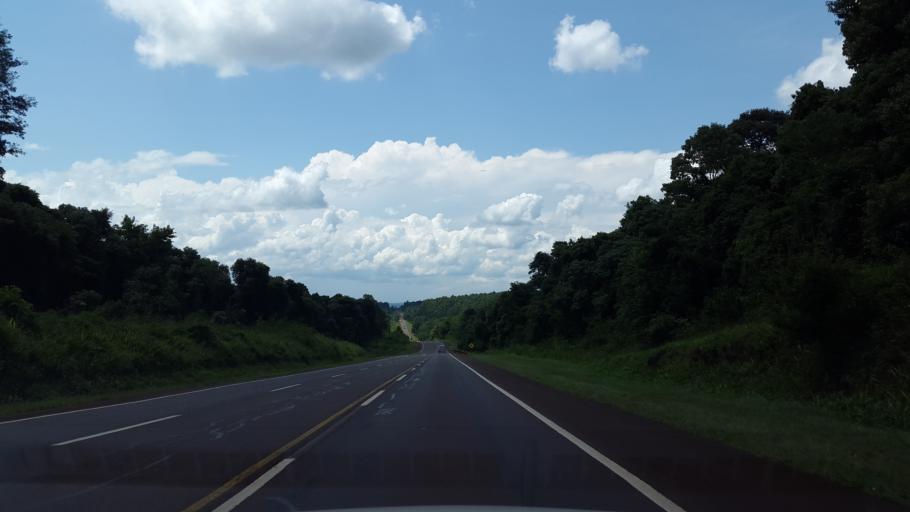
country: AR
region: Misiones
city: El Alcazar
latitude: -26.7136
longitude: -54.8509
